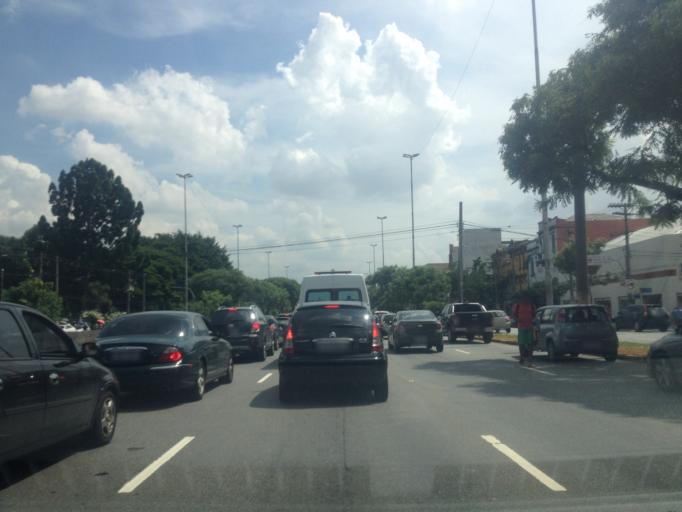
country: BR
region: Sao Paulo
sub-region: Sao Paulo
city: Sao Paulo
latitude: -23.5347
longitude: -46.6333
